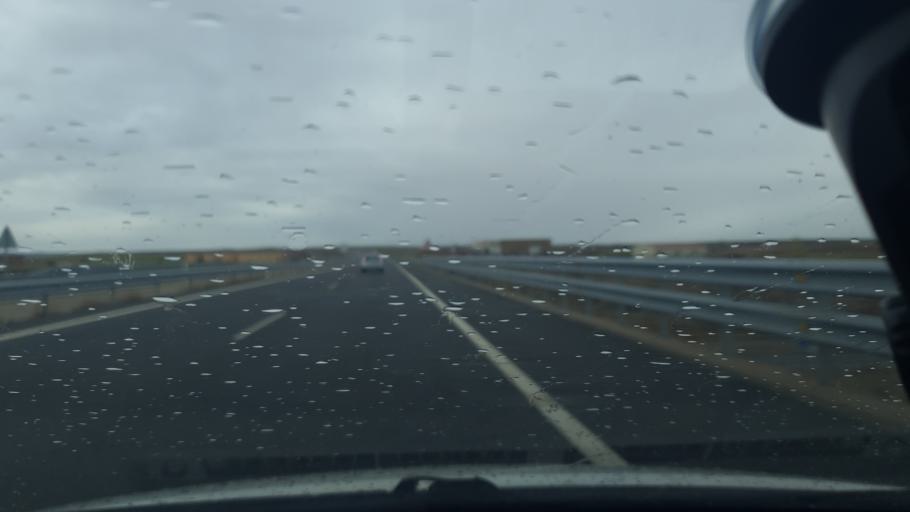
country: ES
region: Castille and Leon
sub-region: Provincia de Segovia
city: Encinillas
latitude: 41.0022
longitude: -4.1534
